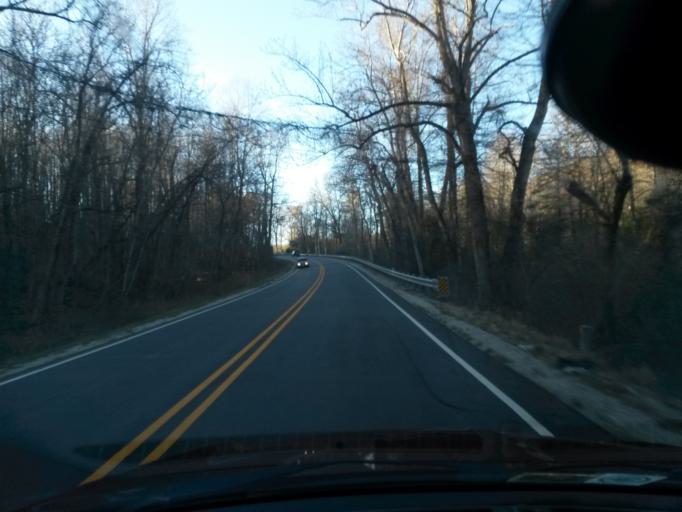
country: US
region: Virginia
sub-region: Amherst County
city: Amherst
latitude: 37.6217
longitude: -79.1064
